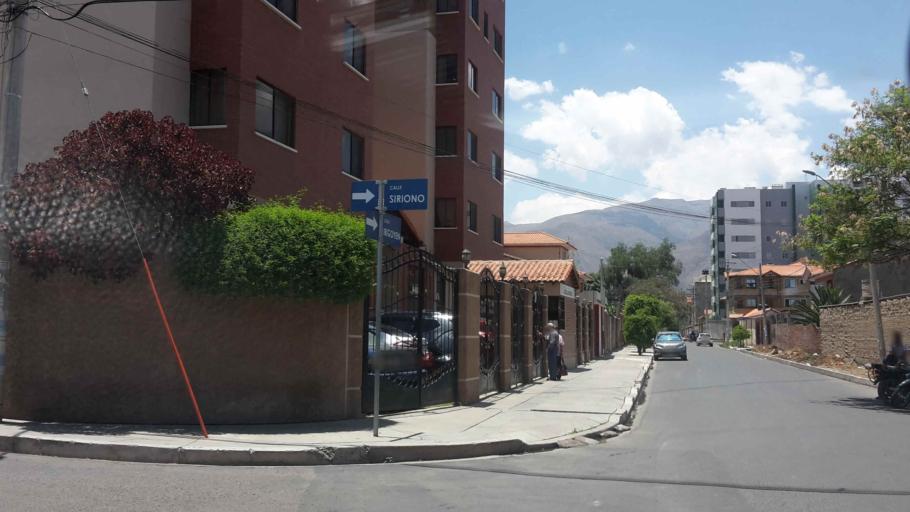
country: BO
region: Cochabamba
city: Cochabamba
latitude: -17.3844
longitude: -66.1843
